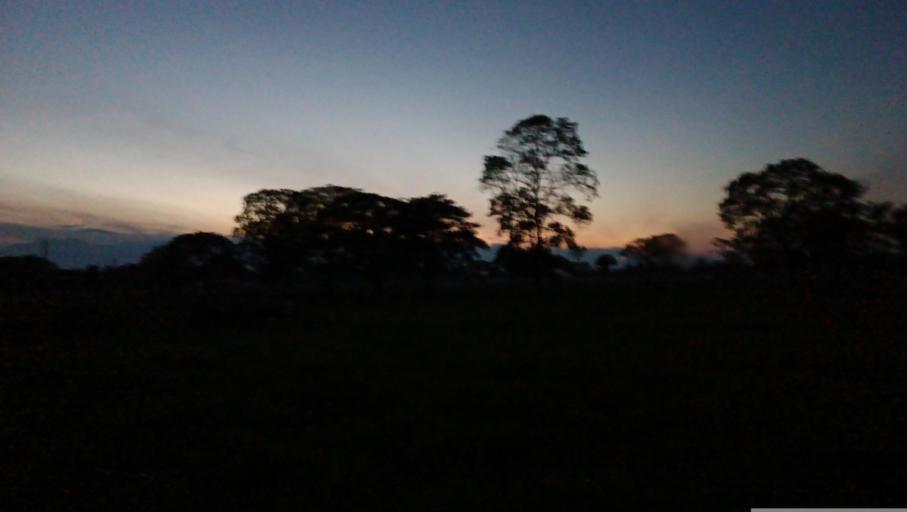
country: CO
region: Arauca
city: Municipio de Fortul
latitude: 6.7228
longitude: -71.6396
